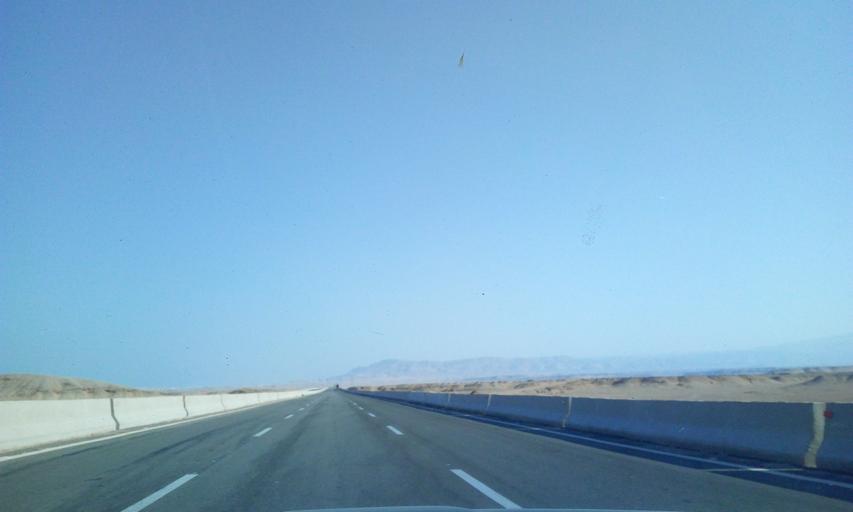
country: EG
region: As Suways
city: Ain Sukhna
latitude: 29.1441
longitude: 32.5183
